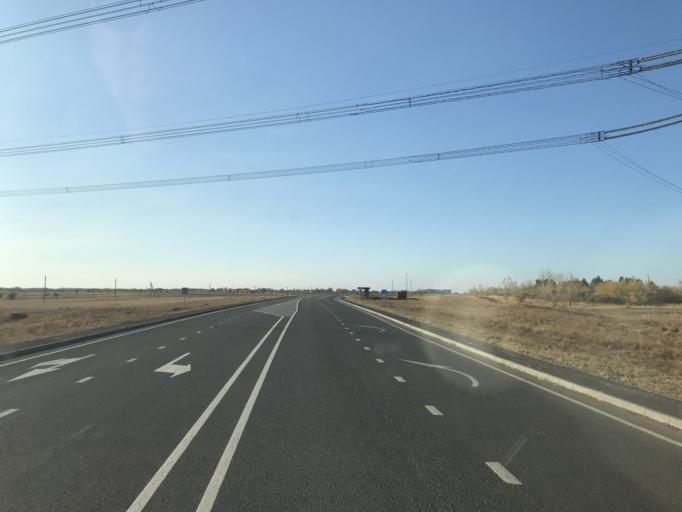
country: KZ
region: Pavlodar
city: Koktobe
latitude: 51.9095
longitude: 77.3579
